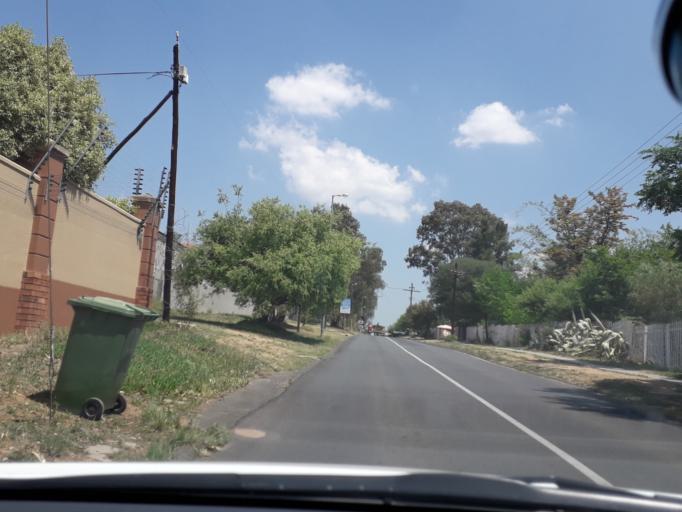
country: ZA
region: Gauteng
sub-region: City of Johannesburg Metropolitan Municipality
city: Midrand
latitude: -26.0249
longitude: 28.0707
